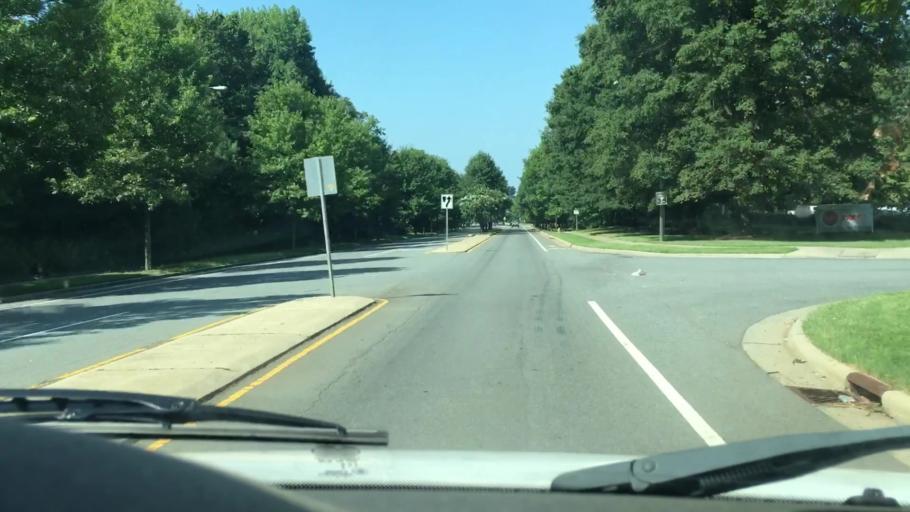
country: US
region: North Carolina
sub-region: Mecklenburg County
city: Charlotte
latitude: 35.2188
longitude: -80.9169
